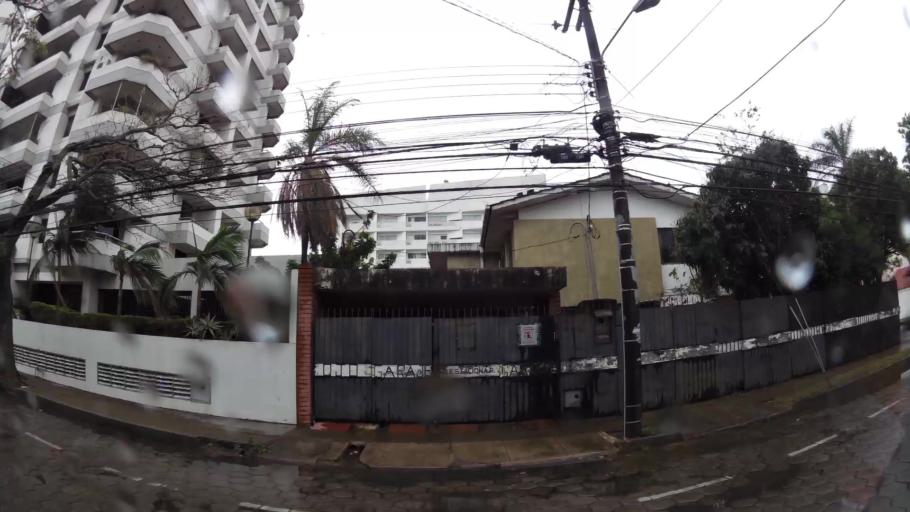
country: BO
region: Santa Cruz
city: Santa Cruz de la Sierra
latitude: -17.7958
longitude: -63.1793
